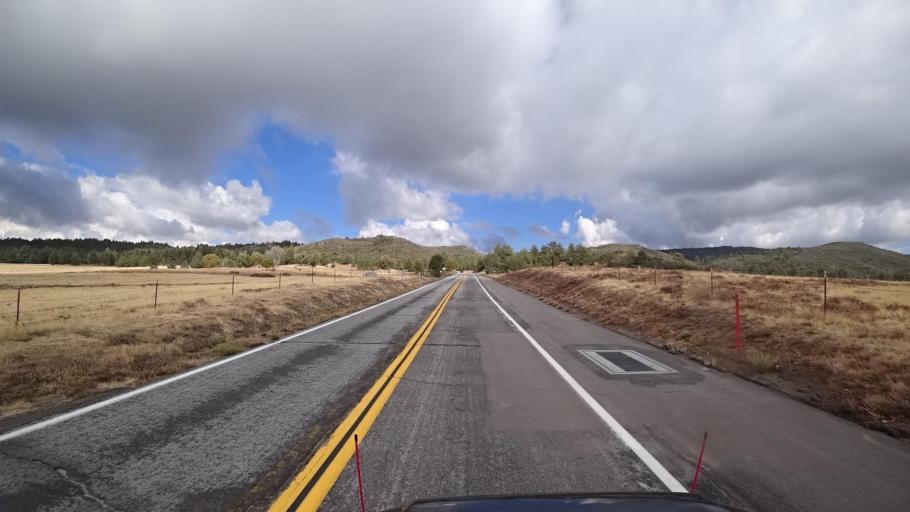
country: US
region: California
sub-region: San Diego County
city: Pine Valley
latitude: 32.8552
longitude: -116.4746
